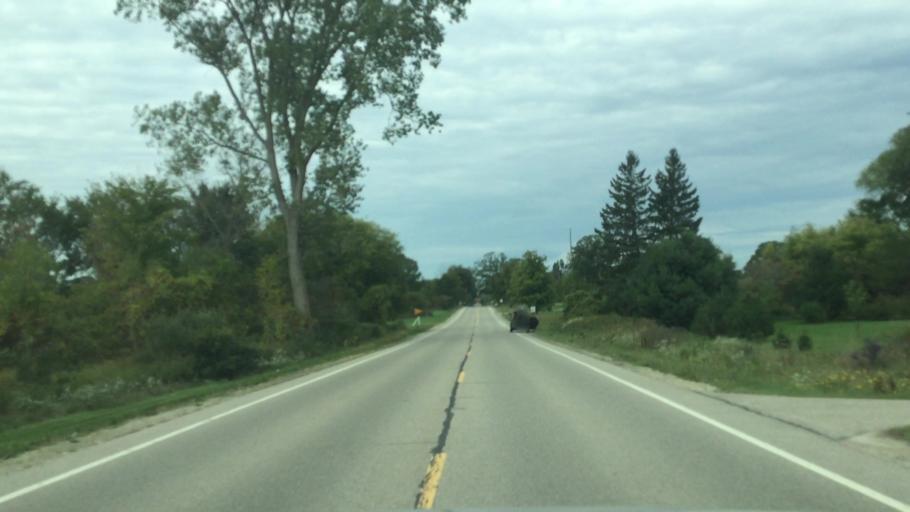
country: US
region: Michigan
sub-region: Livingston County
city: Howell
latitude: 42.6741
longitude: -83.8685
